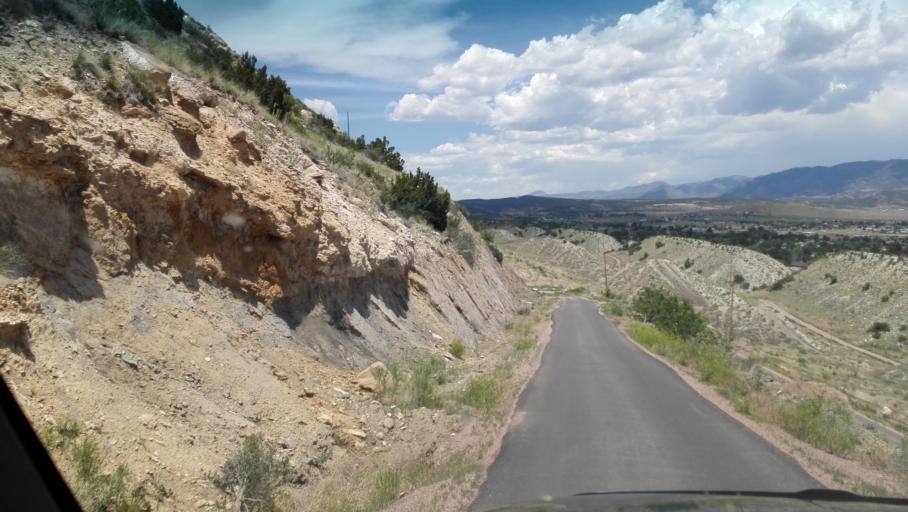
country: US
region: Colorado
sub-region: Fremont County
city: Canon City
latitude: 38.4487
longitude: -105.2480
